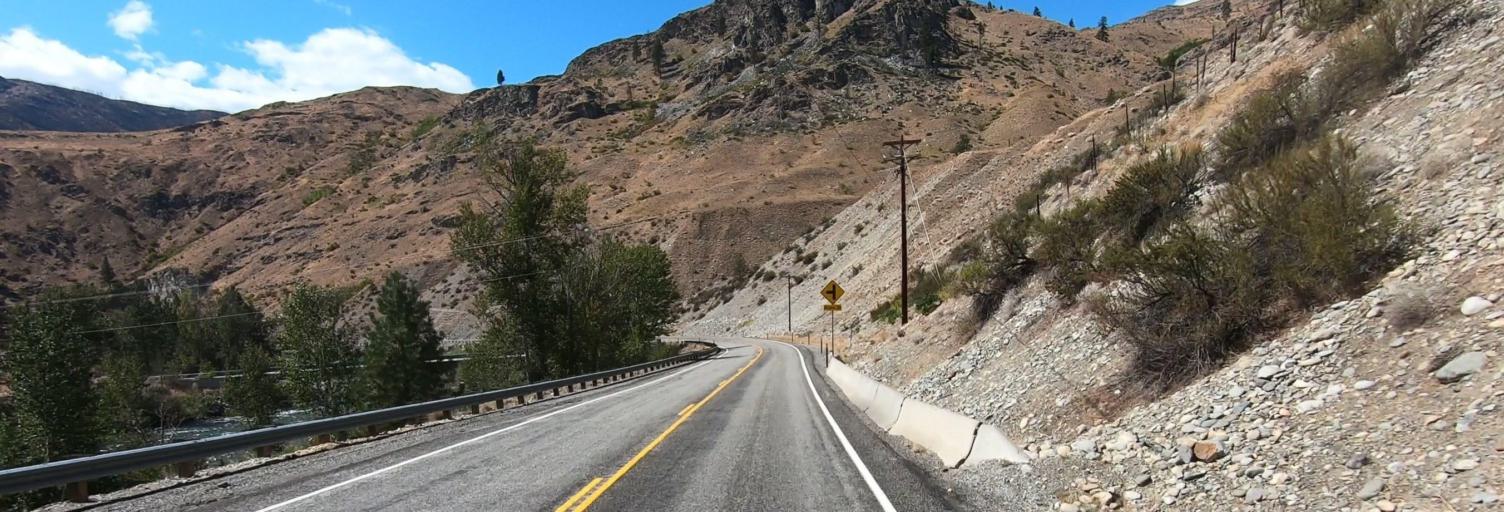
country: US
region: Washington
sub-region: Okanogan County
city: Brewster
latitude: 48.1014
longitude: -120.0188
